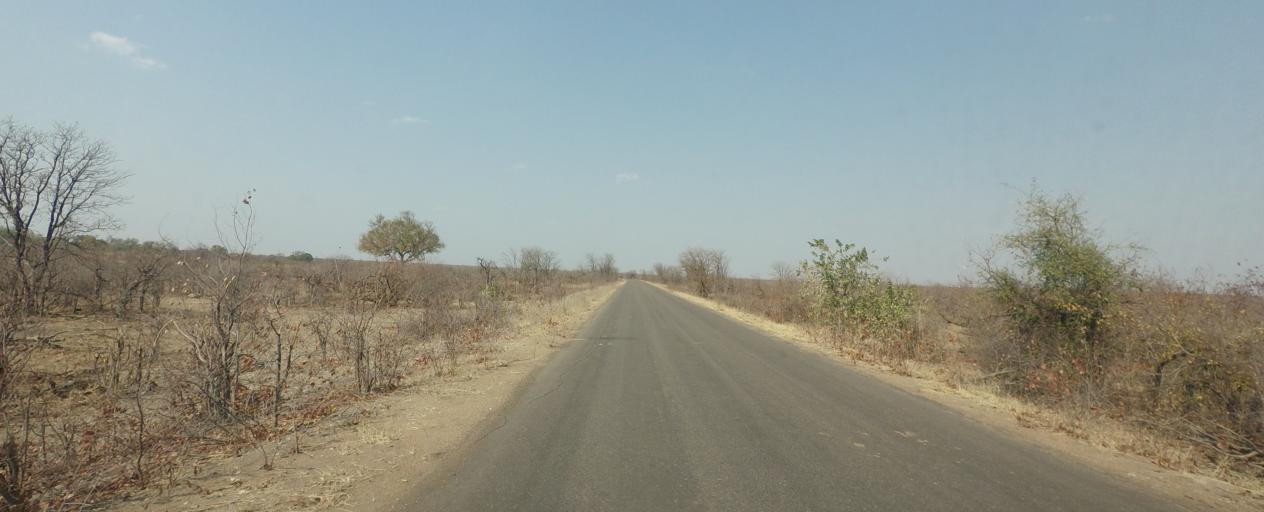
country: ZA
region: Limpopo
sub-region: Mopani District Municipality
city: Giyani
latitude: -23.1675
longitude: 31.3413
